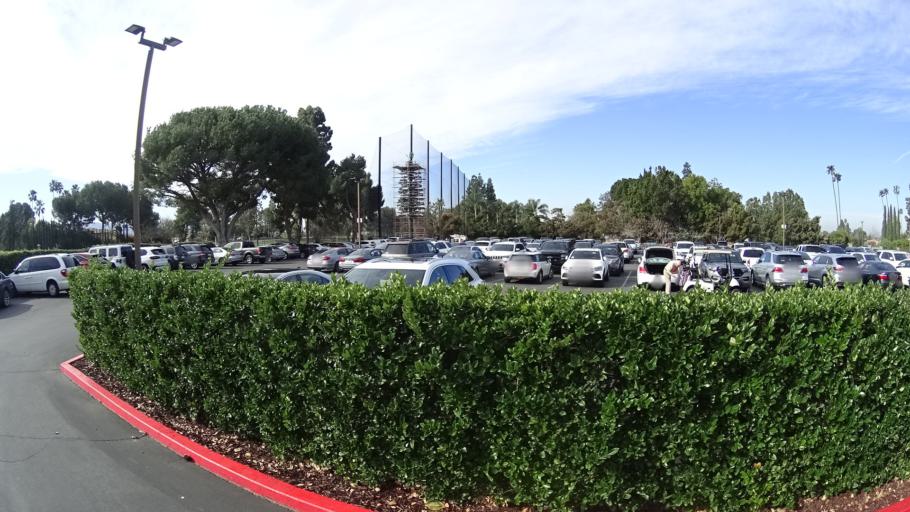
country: US
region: California
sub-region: Orange County
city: Yorba Linda
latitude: 33.8767
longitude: -117.7947
